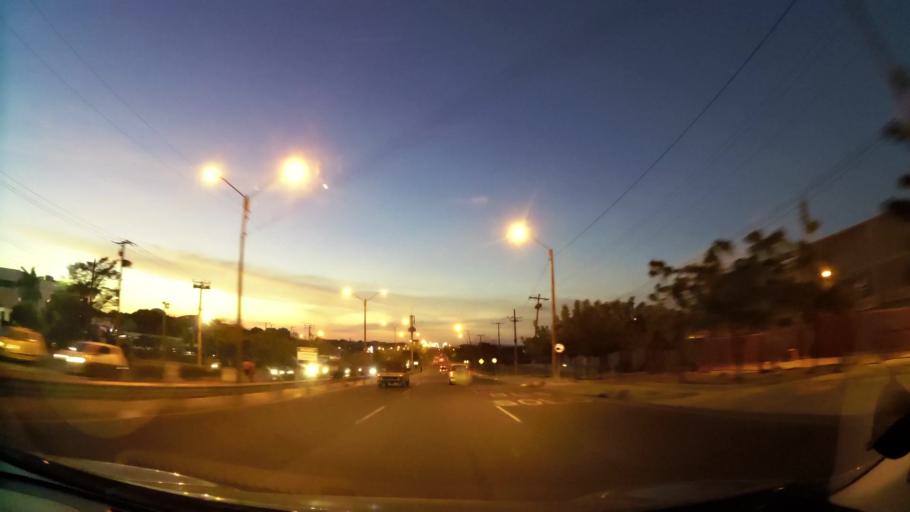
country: CO
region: Atlantico
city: Soledad
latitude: 10.9256
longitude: -74.8224
